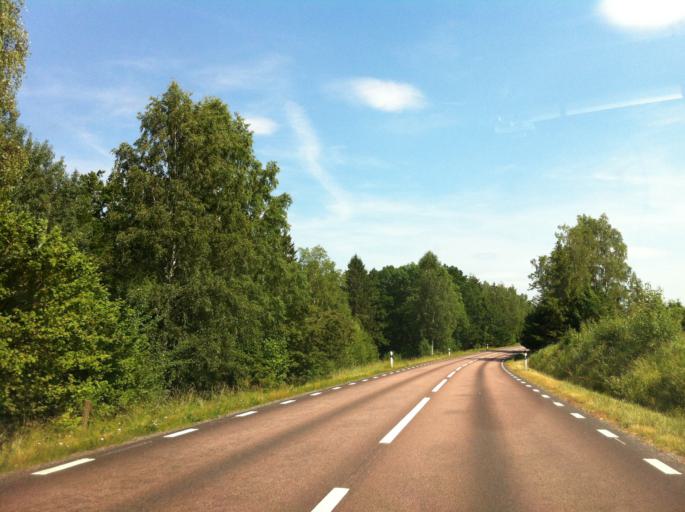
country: SE
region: Kalmar
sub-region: Nybro Kommun
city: Nybro
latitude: 56.7809
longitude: 15.8303
